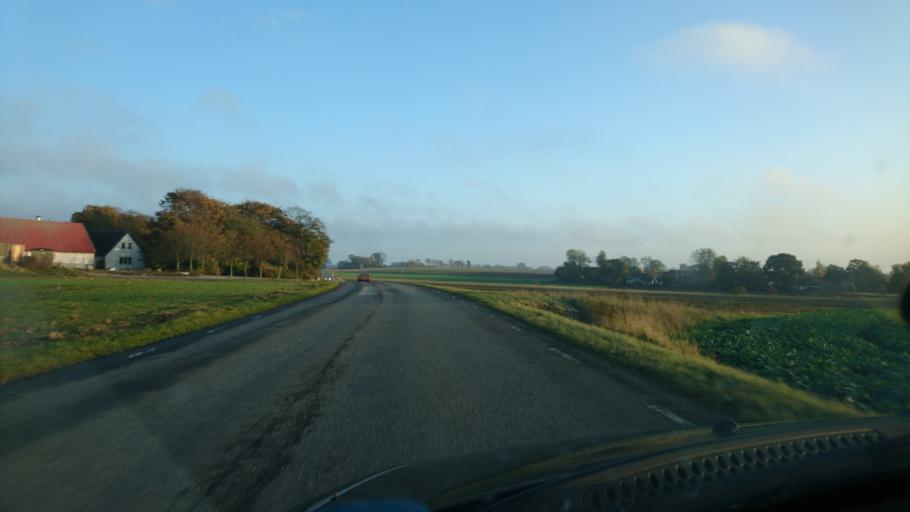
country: SE
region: Skane
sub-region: Tomelilla Kommun
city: Tomelilla
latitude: 55.4632
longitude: 14.0998
